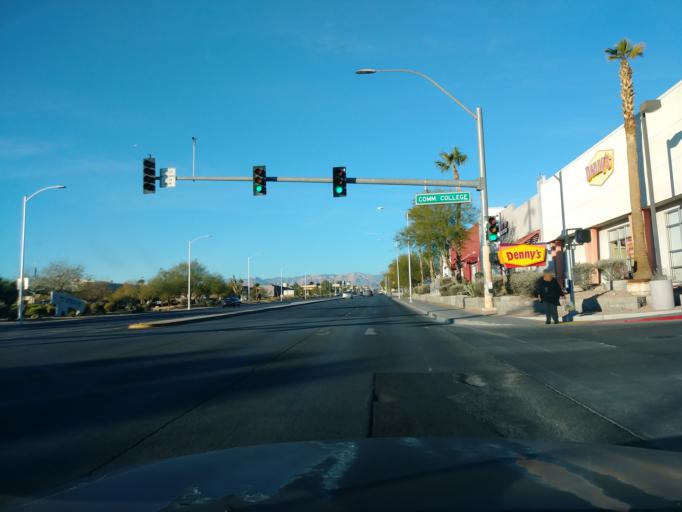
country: US
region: Nevada
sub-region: Clark County
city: Spring Valley
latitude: 36.1593
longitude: -115.2304
